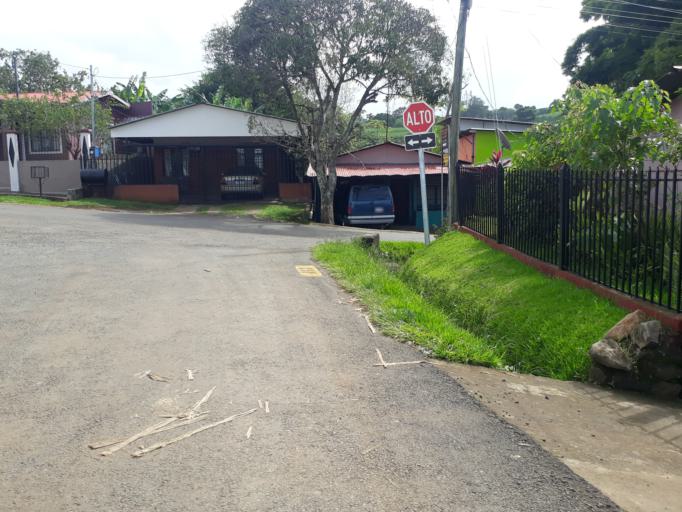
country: CR
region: Alajuela
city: Carrillos
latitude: 10.0273
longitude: -84.3366
